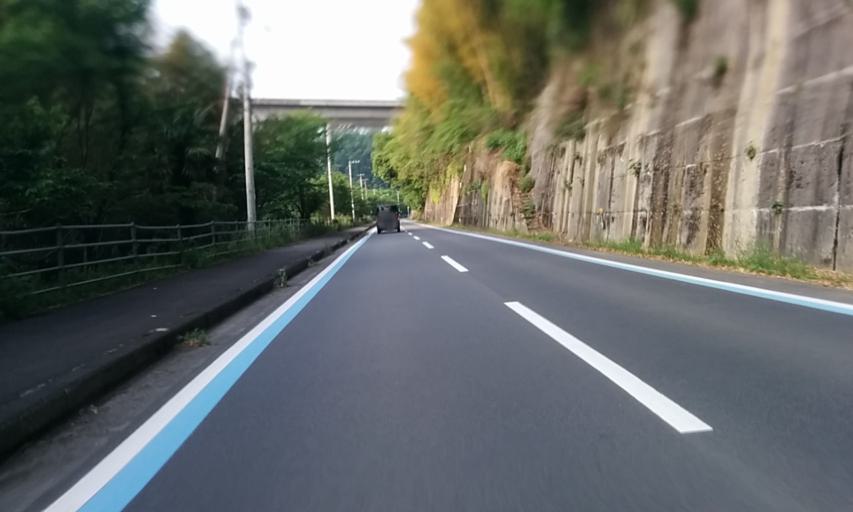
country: JP
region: Ehime
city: Saijo
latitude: 33.8835
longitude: 133.1807
